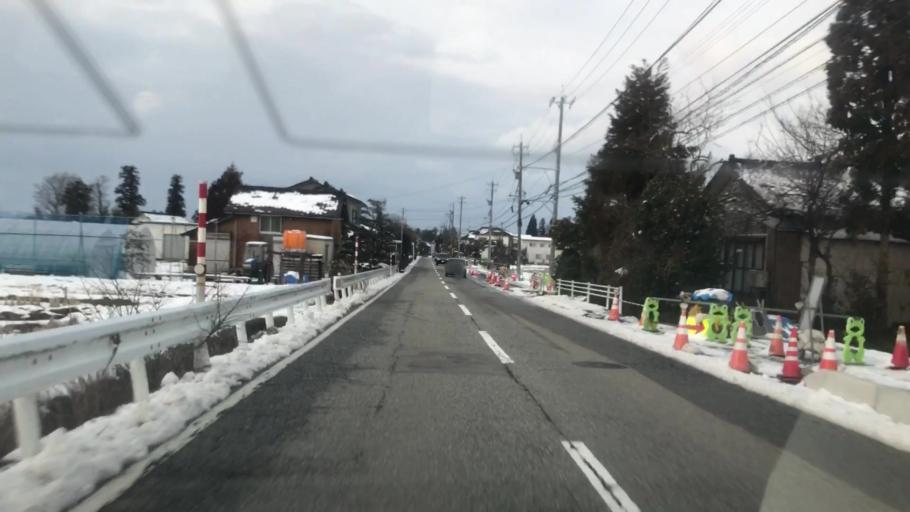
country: JP
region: Toyama
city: Kamiichi
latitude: 36.6897
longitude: 137.3152
